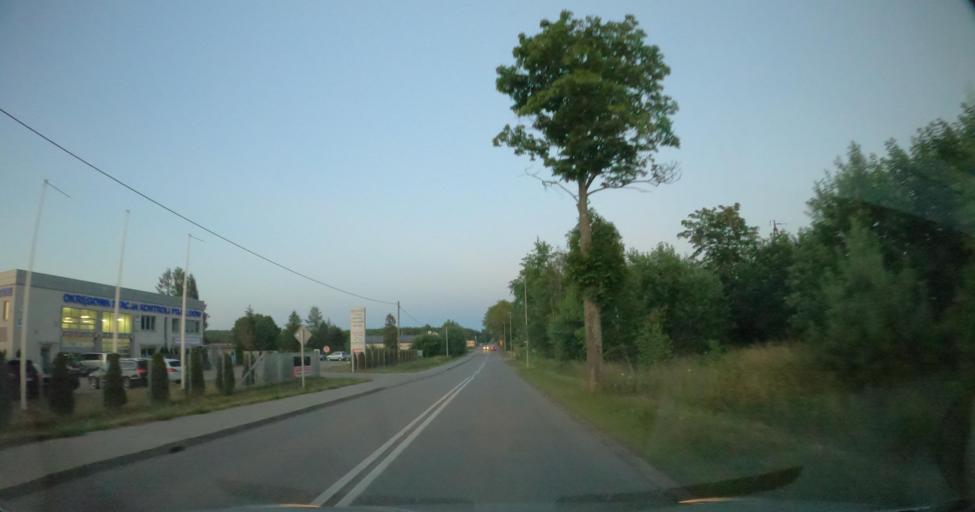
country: PL
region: Pomeranian Voivodeship
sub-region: Powiat wejherowski
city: Szemud
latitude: 54.4848
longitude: 18.2363
